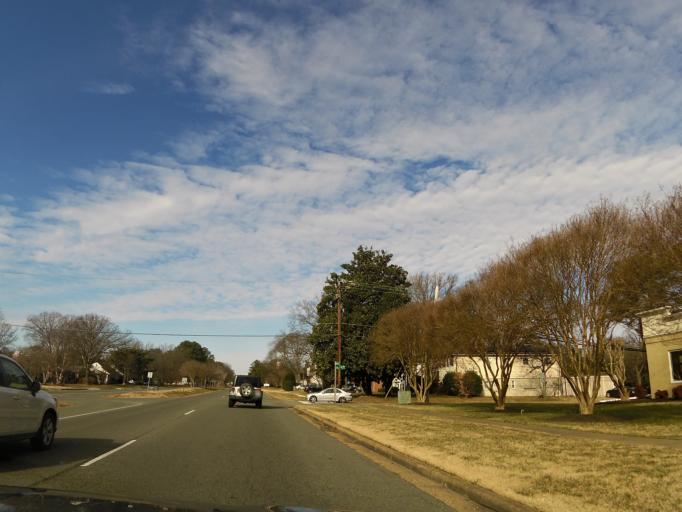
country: US
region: Virginia
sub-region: Henrico County
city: Dumbarton
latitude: 37.5803
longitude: -77.5042
